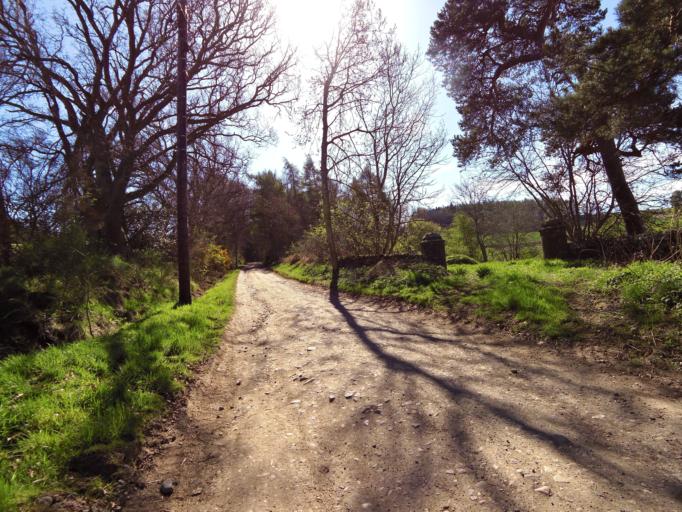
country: GB
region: Scotland
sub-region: Fife
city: Cupar
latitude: 56.3934
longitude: -3.0729
